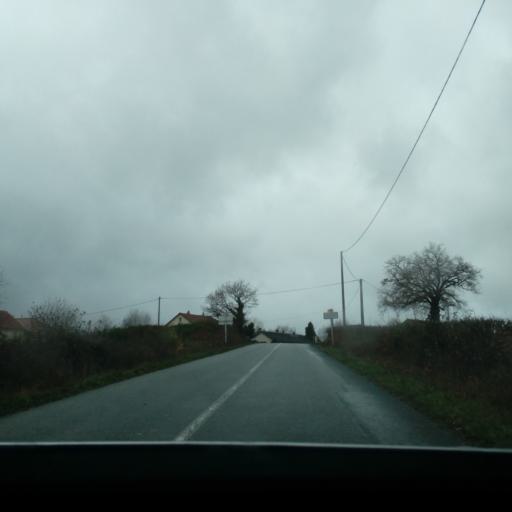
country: FR
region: Limousin
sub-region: Departement de la Creuse
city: Gueret
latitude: 46.1763
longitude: 1.9032
